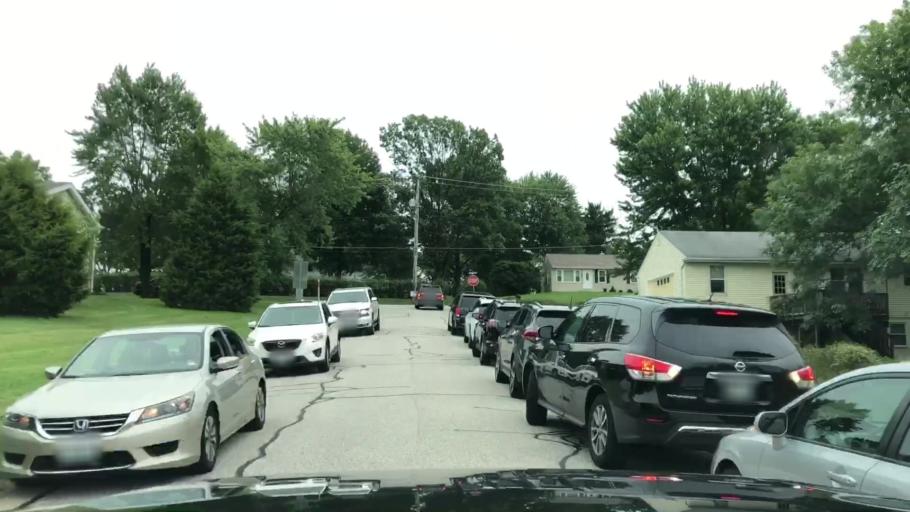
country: US
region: Missouri
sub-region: Saint Louis County
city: Manchester
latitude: 38.5854
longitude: -90.5114
